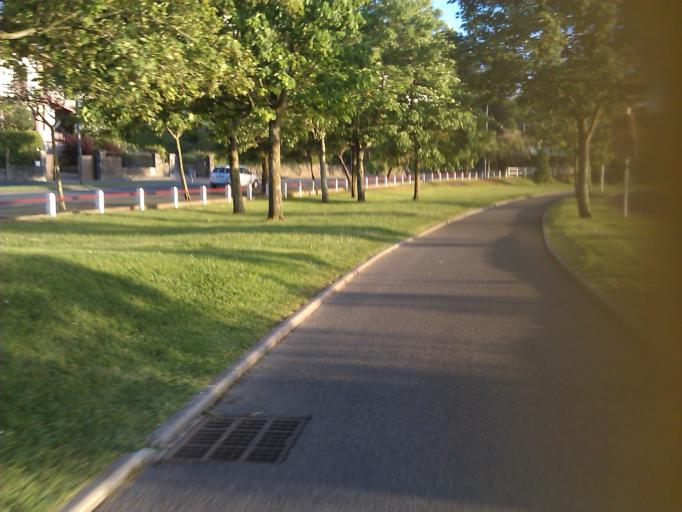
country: FR
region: Aquitaine
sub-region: Departement des Pyrenees-Atlantiques
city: Hendaye
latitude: 43.3650
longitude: -1.7700
